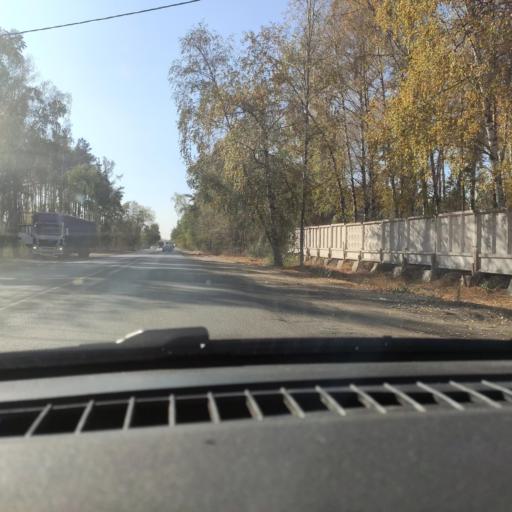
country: RU
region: Voronezj
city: Pridonskoy
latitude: 51.6834
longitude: 39.0973
